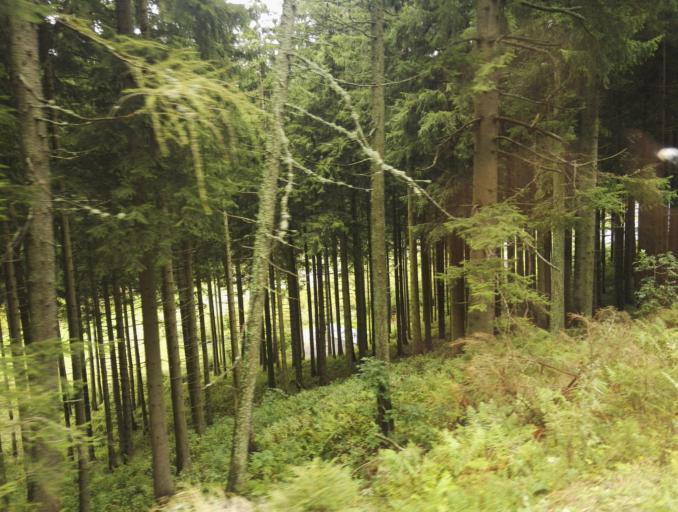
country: AT
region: Styria
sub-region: Politischer Bezirk Leoben
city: Vordernberg
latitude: 47.5170
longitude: 14.9551
